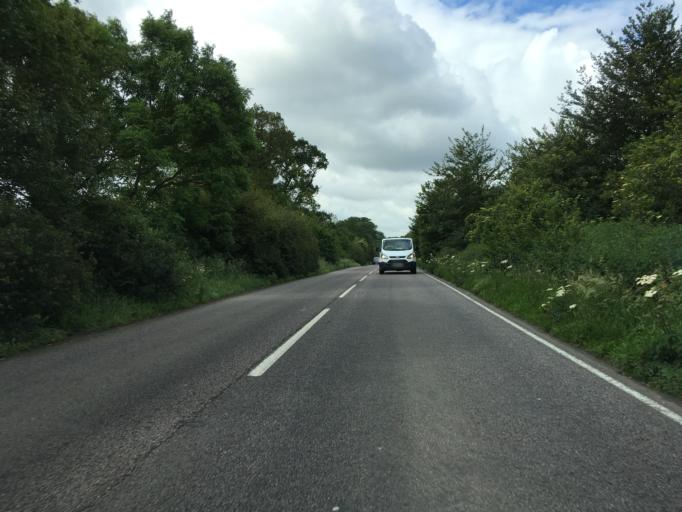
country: GB
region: England
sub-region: Borough of Swindon
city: Highworth
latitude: 51.6153
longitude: -1.7226
